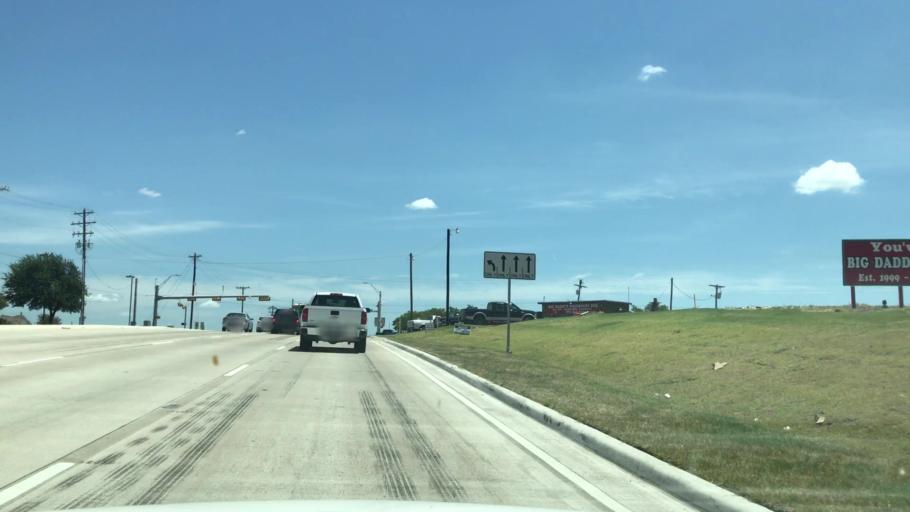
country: US
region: Texas
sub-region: Collin County
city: Lavon
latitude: 33.0222
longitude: -96.4578
